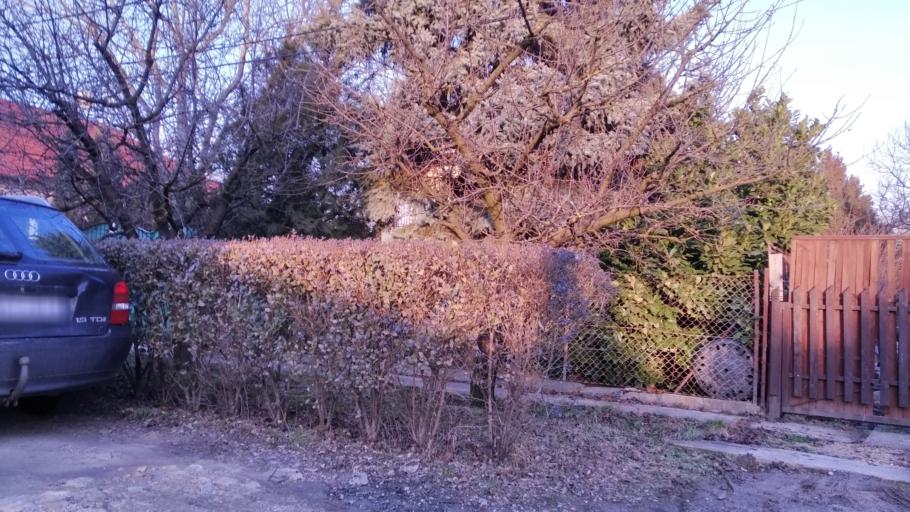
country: HU
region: Pest
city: Budakalasz
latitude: 47.6172
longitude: 19.0361
